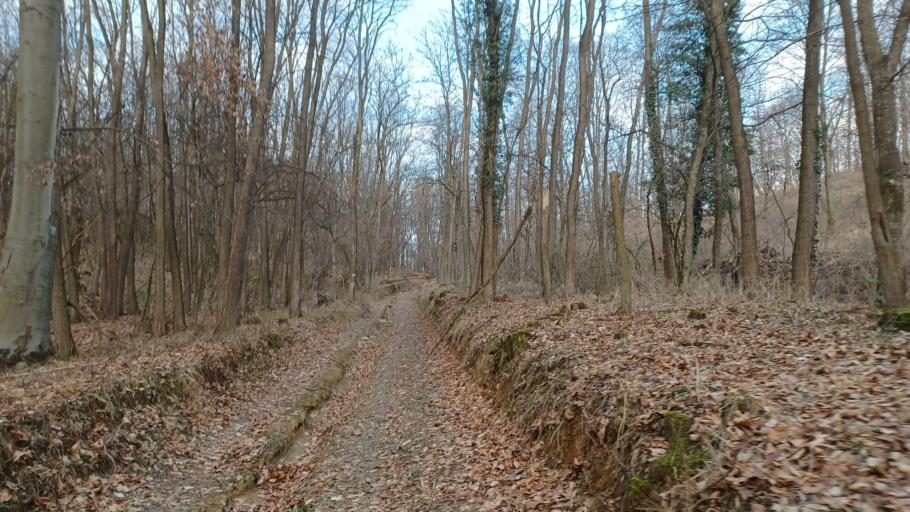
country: HU
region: Tolna
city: Szentgalpuszta
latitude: 46.3086
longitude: 18.6177
